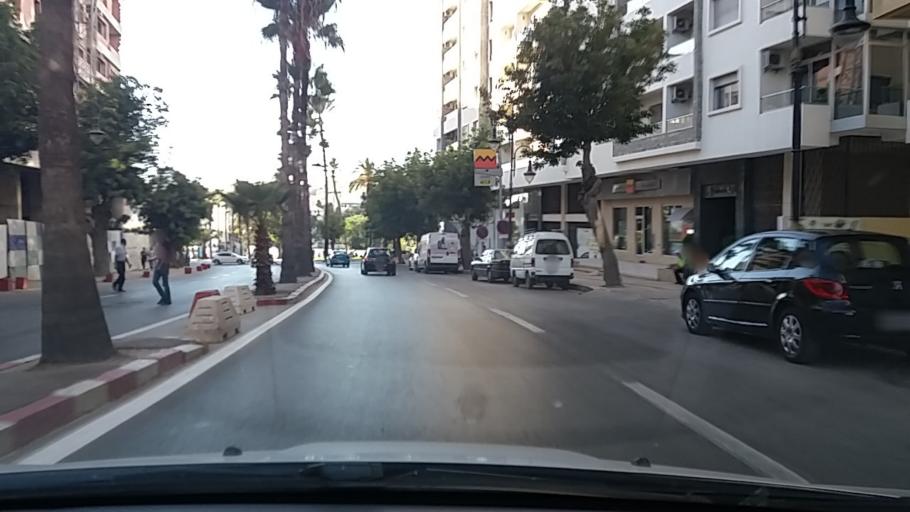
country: MA
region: Tanger-Tetouan
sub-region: Tanger-Assilah
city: Tangier
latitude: 35.7828
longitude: -5.8213
